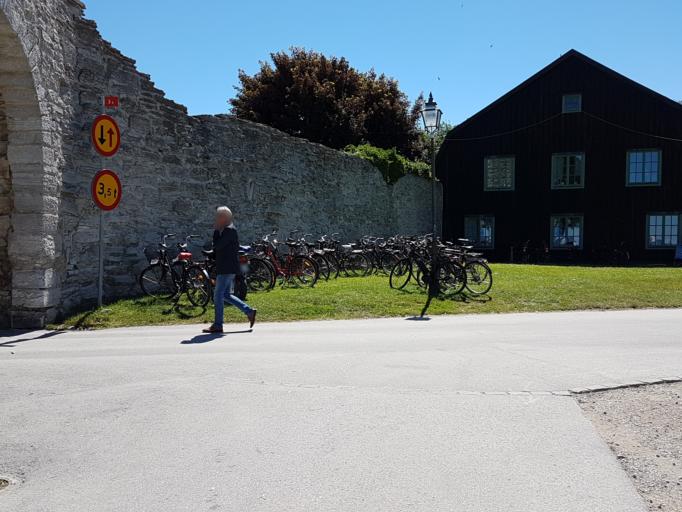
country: SE
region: Gotland
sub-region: Gotland
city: Visby
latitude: 57.6422
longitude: 18.2912
